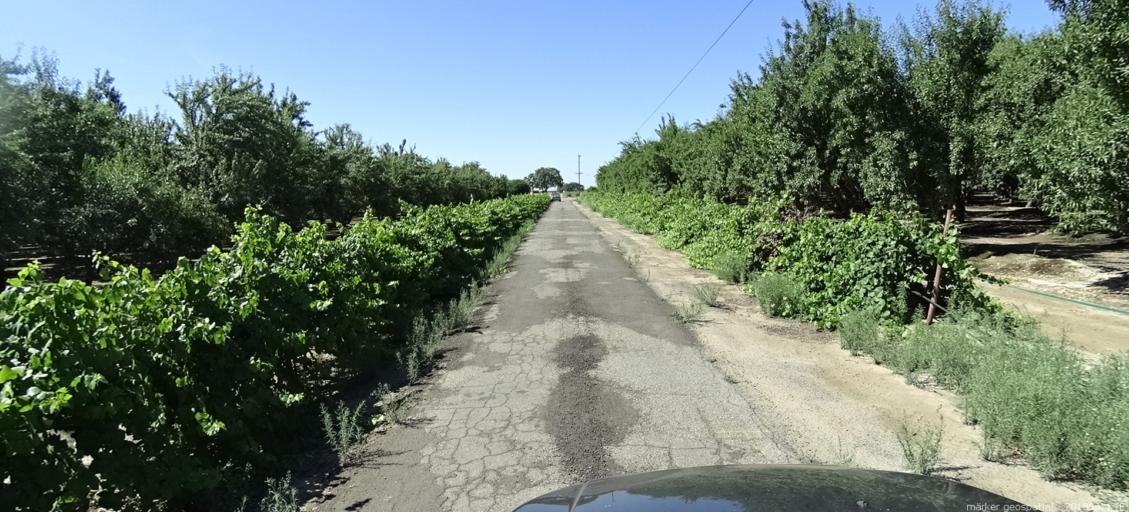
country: US
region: California
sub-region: Madera County
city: Madera
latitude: 36.9503
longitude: -120.1749
